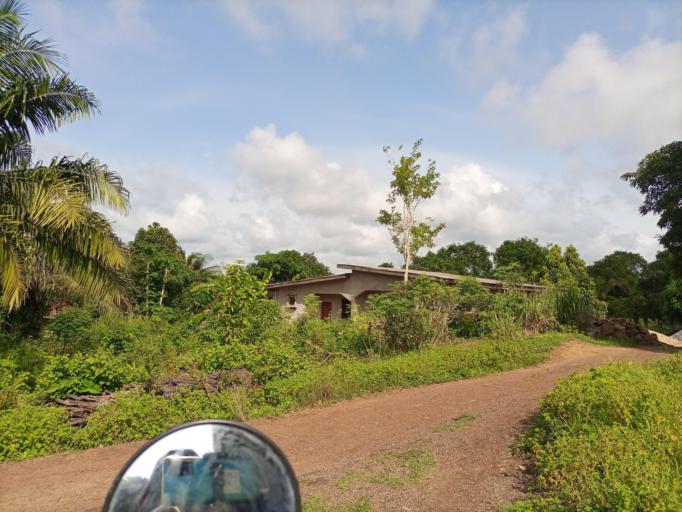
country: SL
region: Southern Province
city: Bo
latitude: 7.9649
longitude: -11.7657
